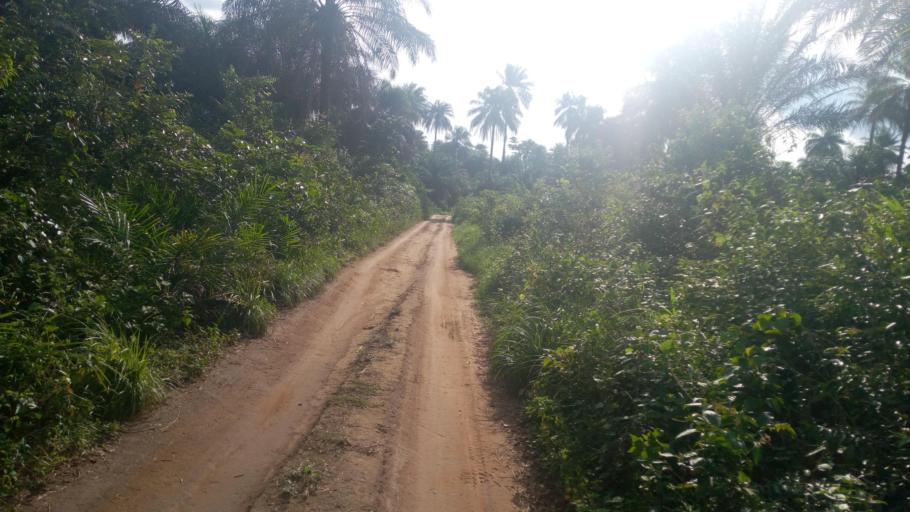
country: SL
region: Southern Province
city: Serabu
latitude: 7.6423
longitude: -12.1579
